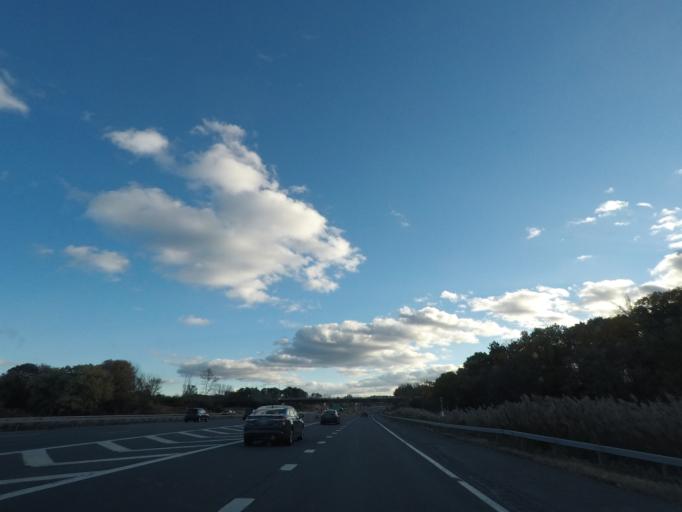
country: US
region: New York
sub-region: Albany County
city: Cohoes
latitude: 42.7657
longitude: -73.7626
